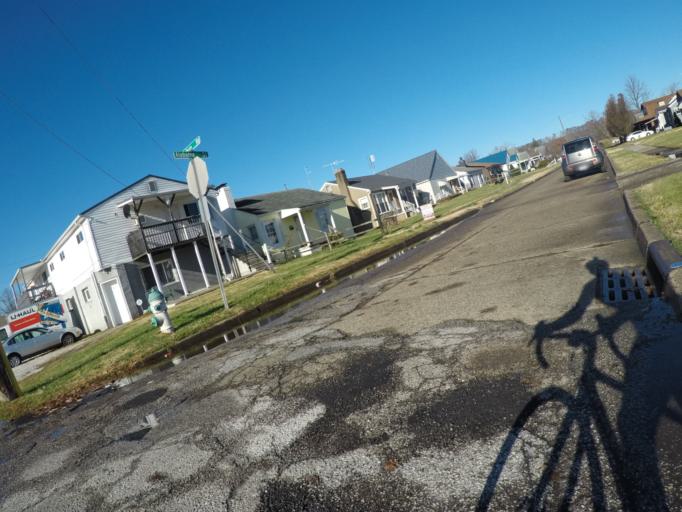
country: US
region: Ohio
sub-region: Lawrence County
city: Burlington
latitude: 38.4032
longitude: -82.5111
